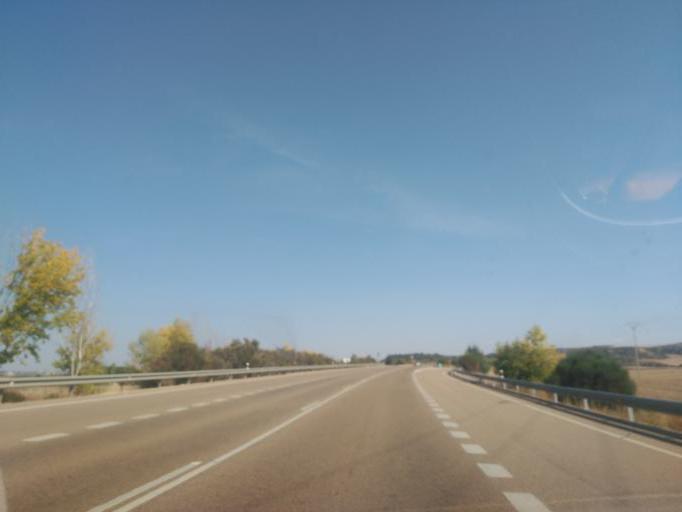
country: ES
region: Castille and Leon
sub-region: Provincia de Valladolid
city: Quintanilla de Arriba
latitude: 41.6203
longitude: -4.2314
